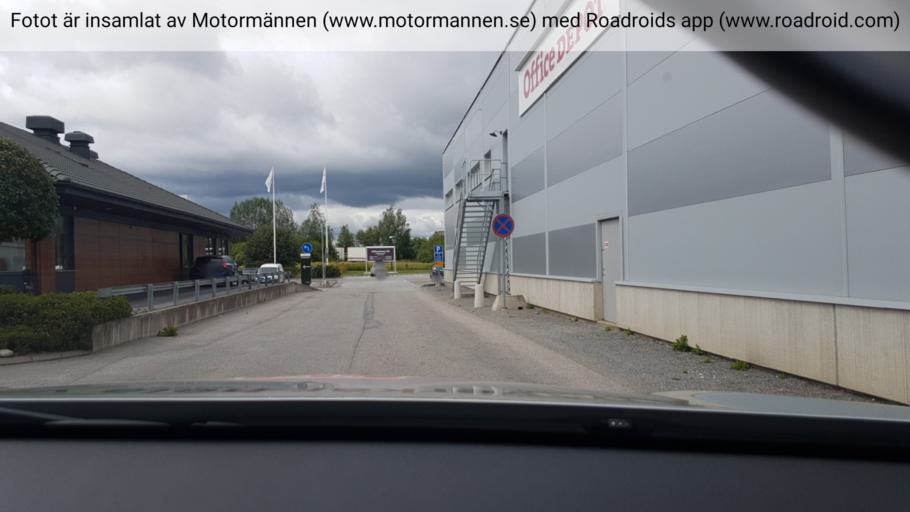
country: SE
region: Stockholm
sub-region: Stockholms Kommun
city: Arsta
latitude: 59.2867
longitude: 18.0506
